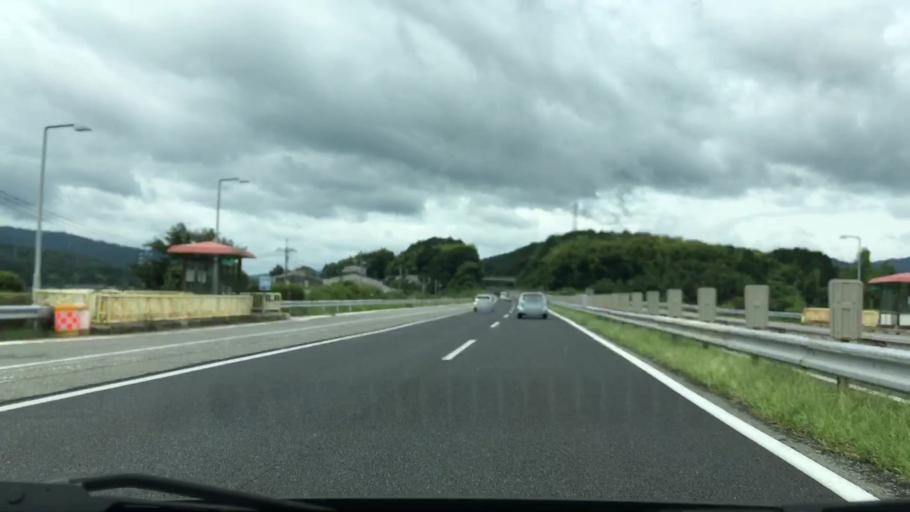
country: JP
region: Okayama
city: Tsuyama
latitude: 35.0627
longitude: 133.8981
